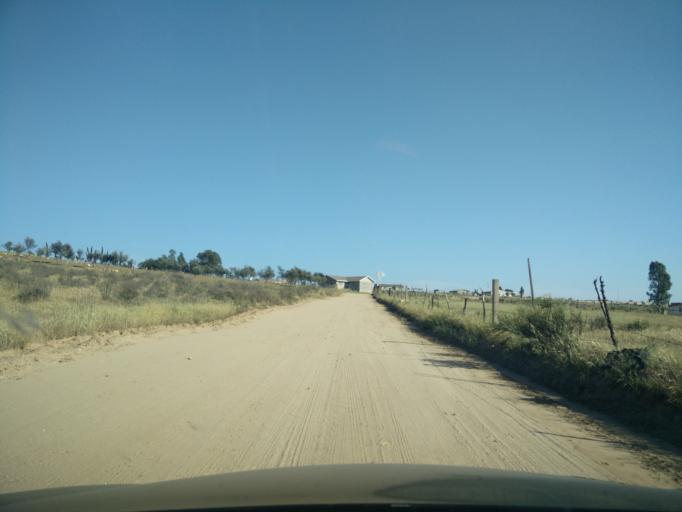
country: MX
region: Baja California
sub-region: Ensenada
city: Rancho Verde
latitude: 32.0460
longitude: -116.6475
